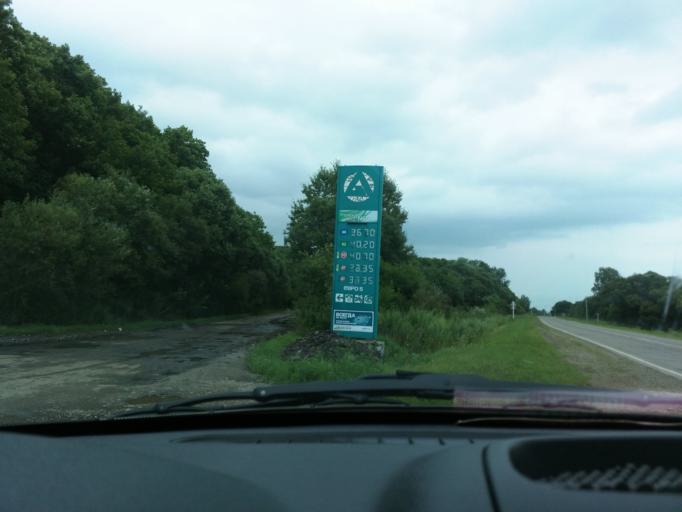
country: RU
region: Primorskiy
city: Novopokrovka
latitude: 45.8589
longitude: 134.5294
